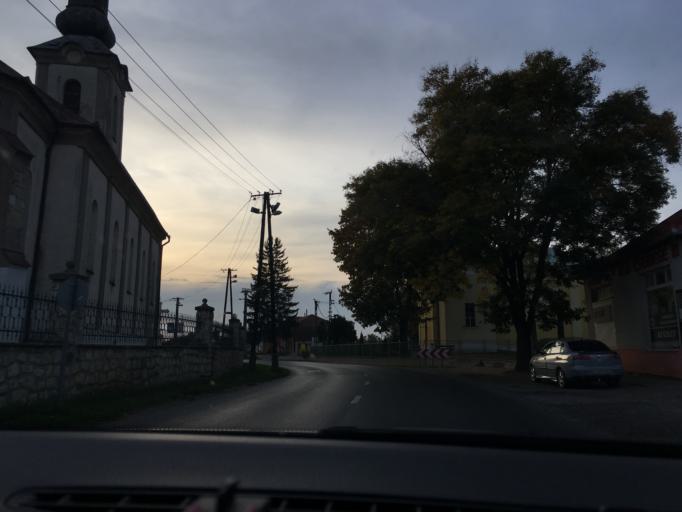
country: HU
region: Szabolcs-Szatmar-Bereg
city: Kallosemjen
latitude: 47.8592
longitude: 21.9245
